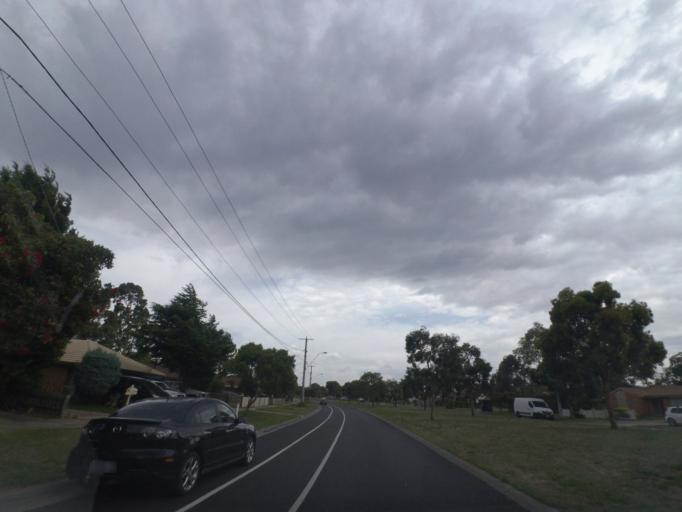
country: AU
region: Victoria
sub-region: Whittlesea
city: Epping
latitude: -37.6407
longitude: 145.0552
